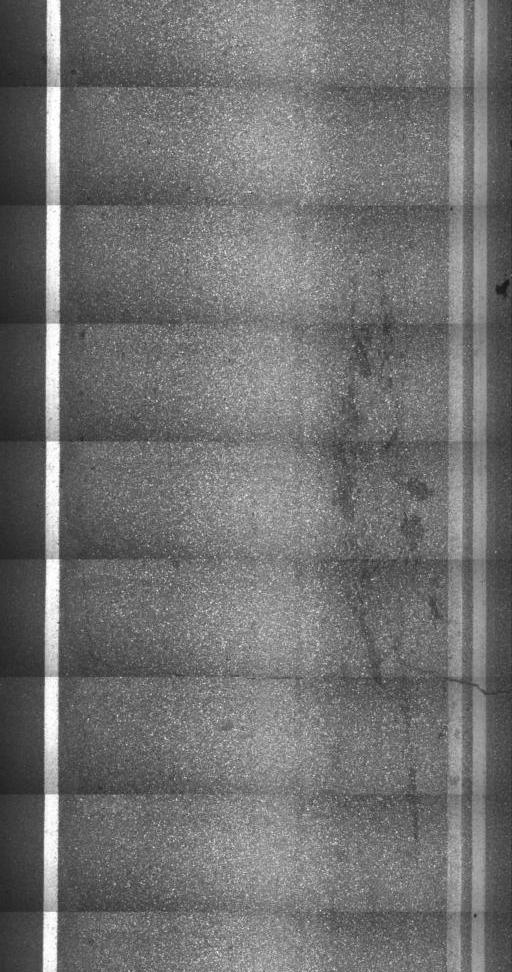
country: US
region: Vermont
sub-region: Chittenden County
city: Williston
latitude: 44.4157
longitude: -72.9991
